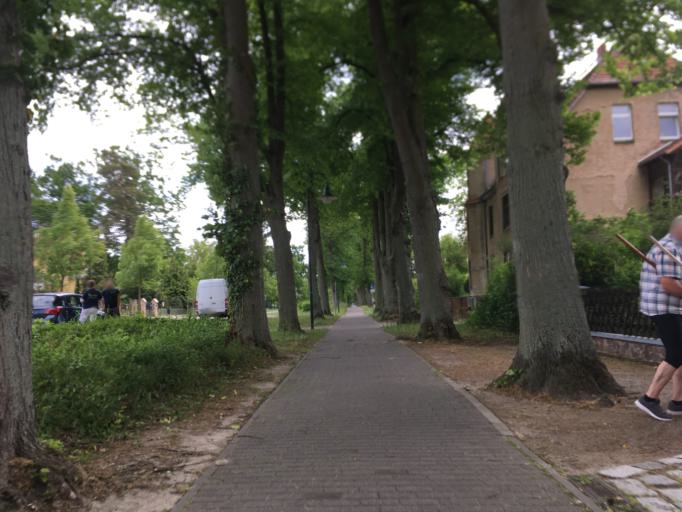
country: DE
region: Brandenburg
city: Biesenthal
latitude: 52.7616
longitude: 13.6541
